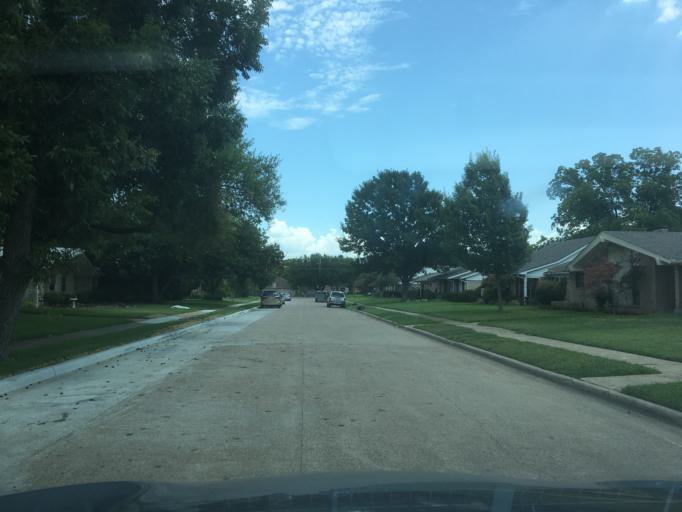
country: US
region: Texas
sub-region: Dallas County
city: Garland
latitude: 32.8683
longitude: -96.6498
